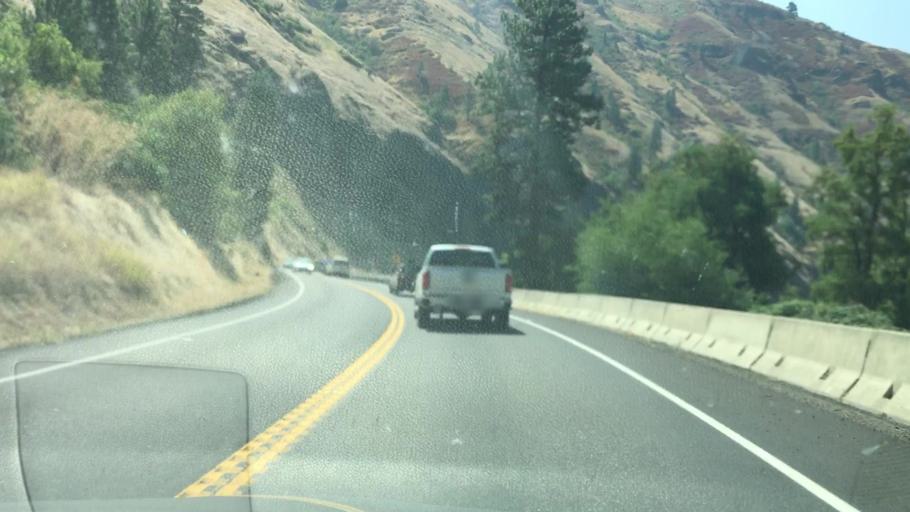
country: US
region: Idaho
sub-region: Nez Perce County
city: Lapwai
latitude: 46.4964
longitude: -116.7256
